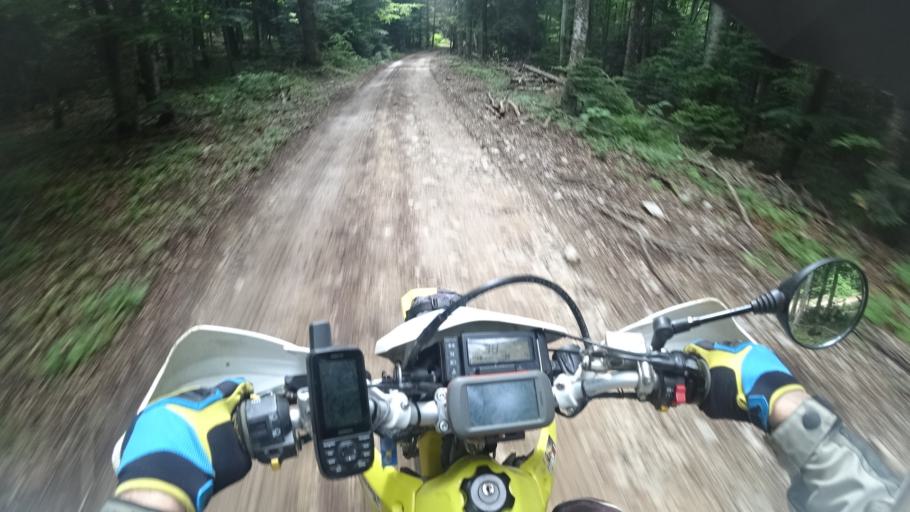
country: BA
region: Federation of Bosnia and Herzegovina
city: Izacic
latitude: 44.7919
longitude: 15.7116
